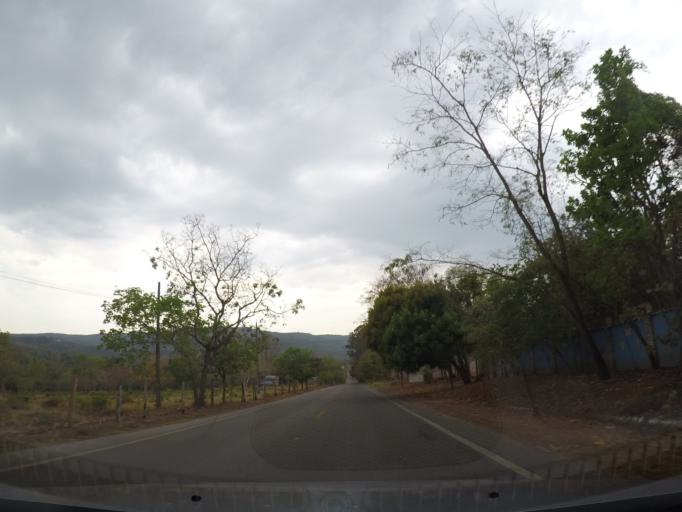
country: BR
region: Goias
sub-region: Pirenopolis
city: Pirenopolis
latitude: -15.8499
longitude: -48.9306
